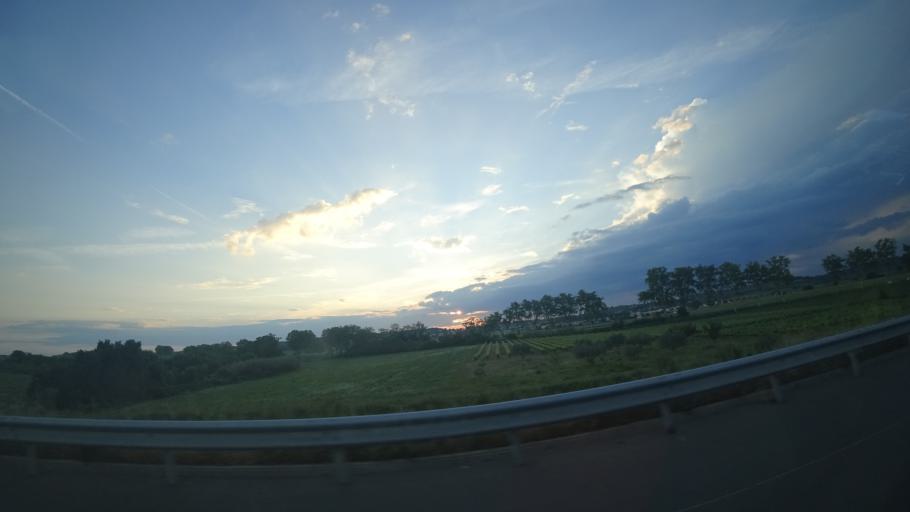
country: FR
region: Languedoc-Roussillon
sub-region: Departement de l'Herault
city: Tourbes
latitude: 43.4384
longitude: 3.3938
